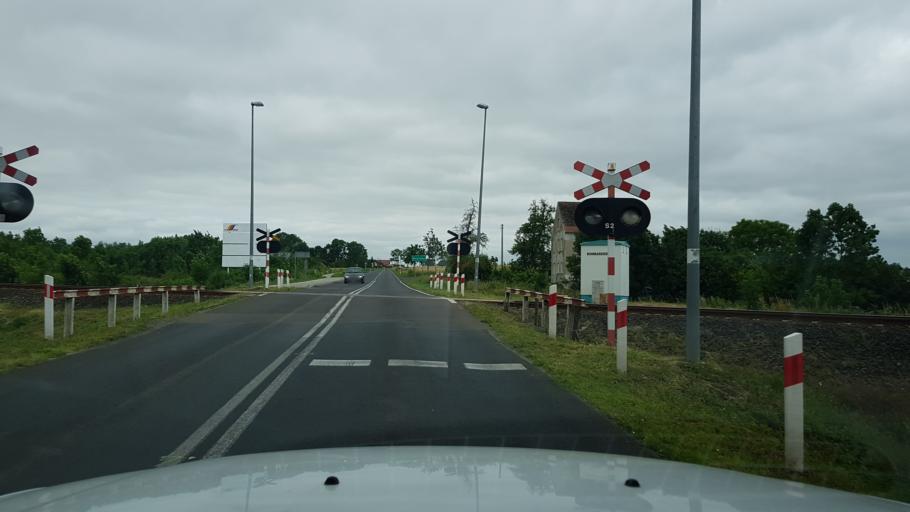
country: PL
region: West Pomeranian Voivodeship
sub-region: Powiat gryficki
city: Gryfice
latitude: 53.9075
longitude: 15.1844
